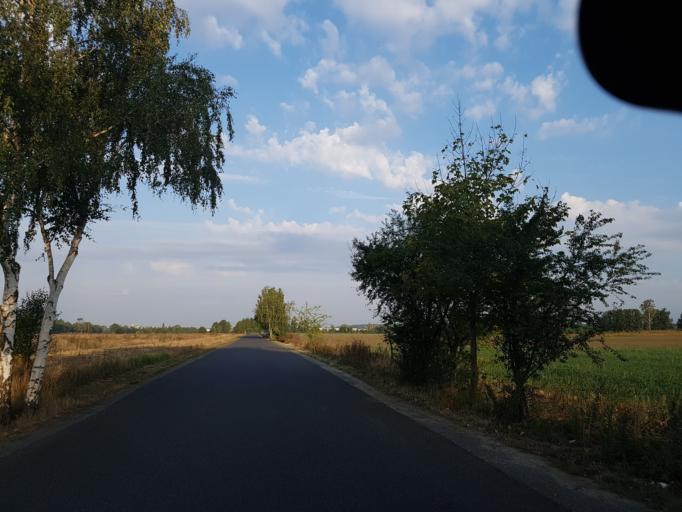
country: DE
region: Brandenburg
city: Elsterwerda
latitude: 51.4565
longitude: 13.5554
